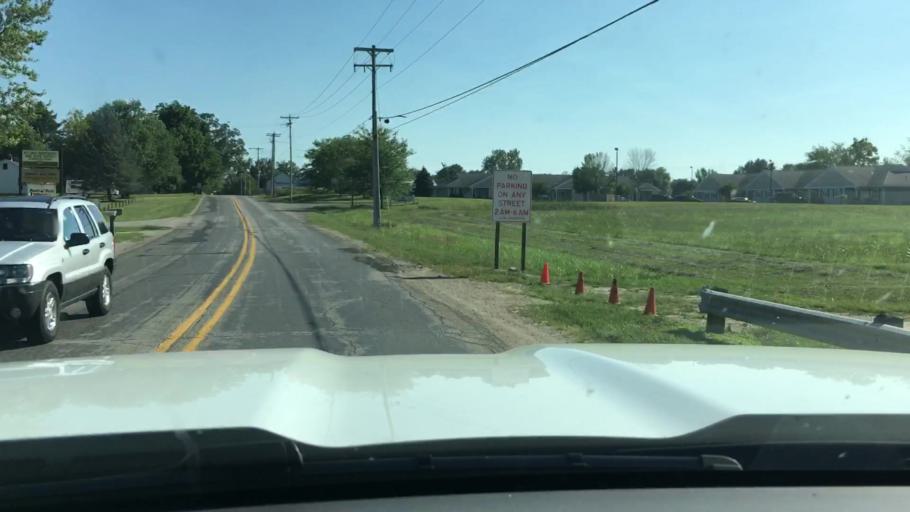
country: US
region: Michigan
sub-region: Muskegon County
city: Ravenna
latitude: 43.1965
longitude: -85.9367
